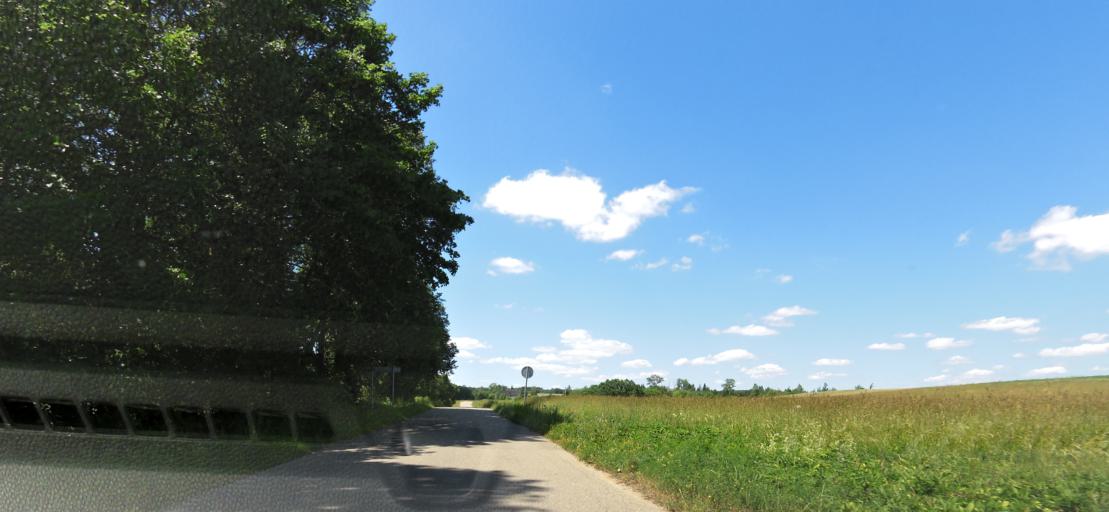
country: LT
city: Nemencine
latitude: 54.8759
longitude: 25.5395
